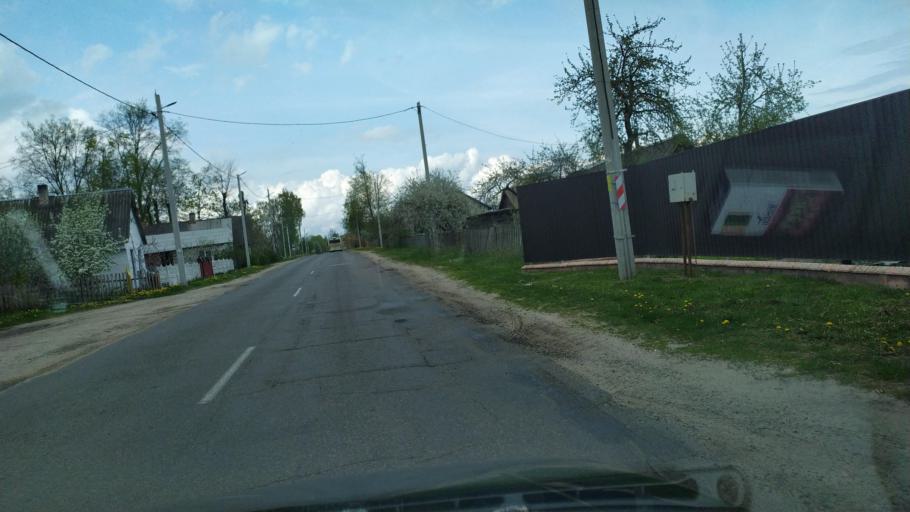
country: BY
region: Brest
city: Pruzhany
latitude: 52.5830
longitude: 24.4116
